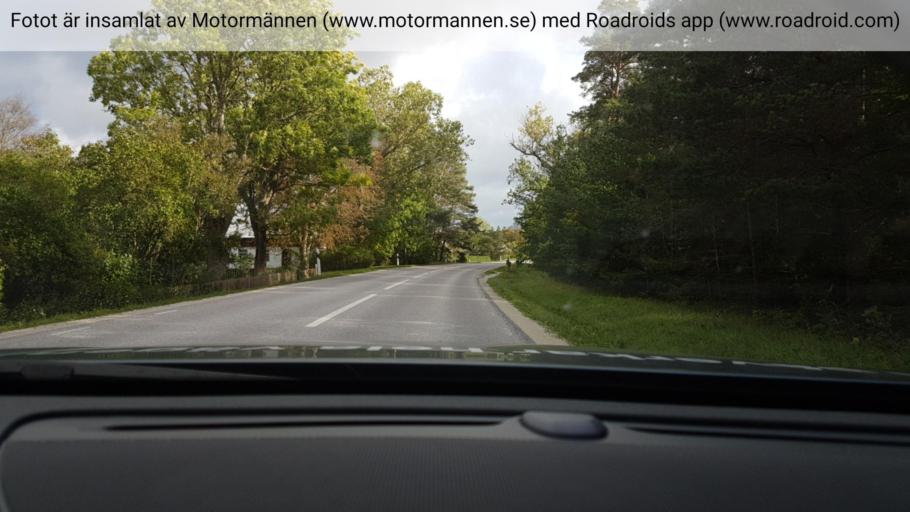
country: SE
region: Gotland
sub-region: Gotland
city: Visby
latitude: 57.6750
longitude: 18.4857
